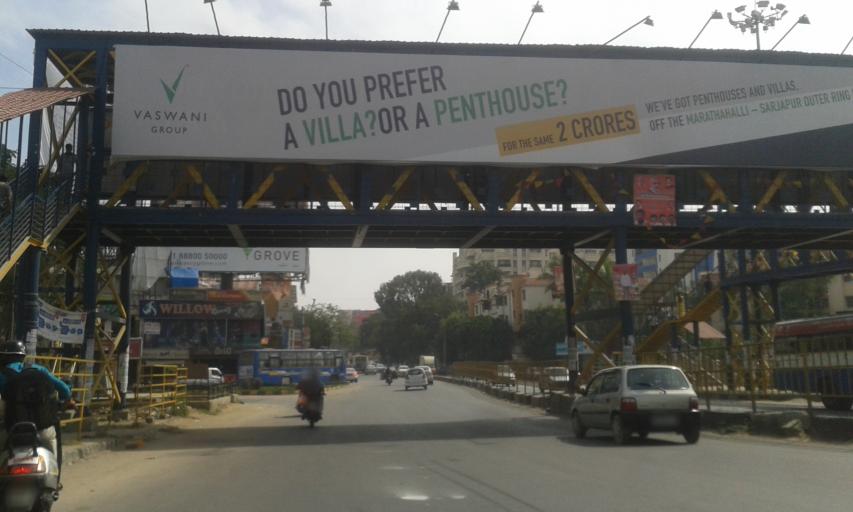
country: IN
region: Karnataka
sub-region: Bangalore Urban
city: Bangalore
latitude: 12.9564
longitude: 77.7090
